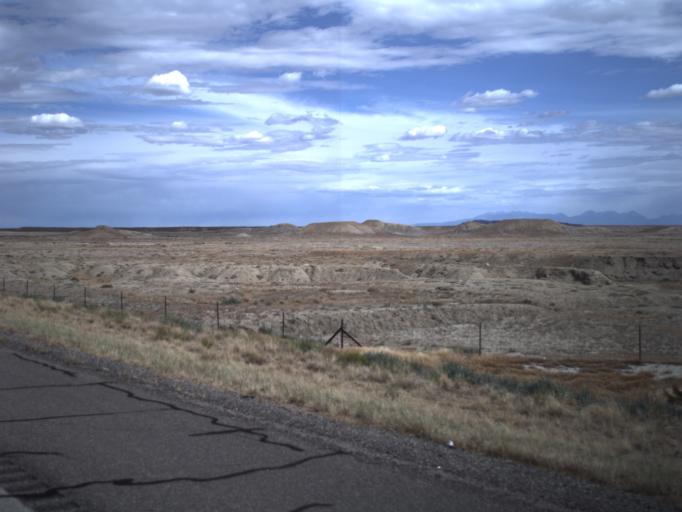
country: US
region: Utah
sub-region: Grand County
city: Moab
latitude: 38.9265
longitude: -109.8989
